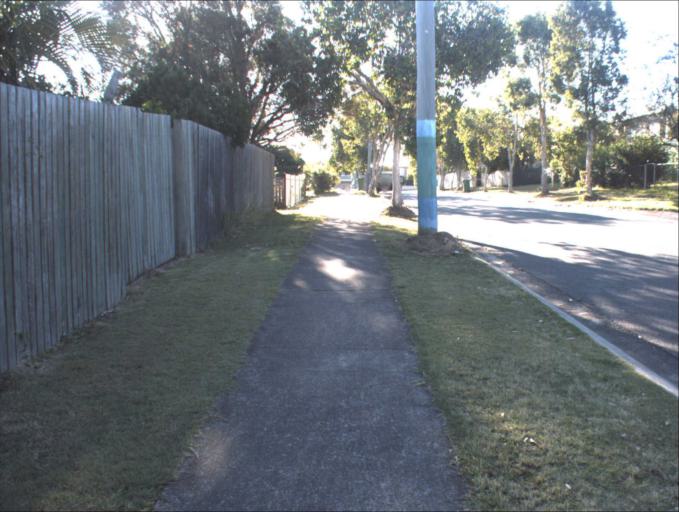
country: AU
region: Queensland
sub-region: Logan
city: Logan City
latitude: -27.6410
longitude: 153.1178
